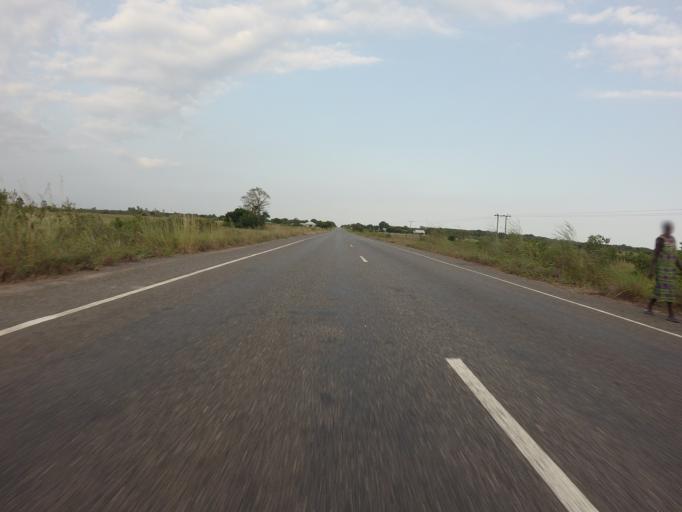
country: GH
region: Volta
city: Anloga
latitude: 6.0888
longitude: 0.5375
